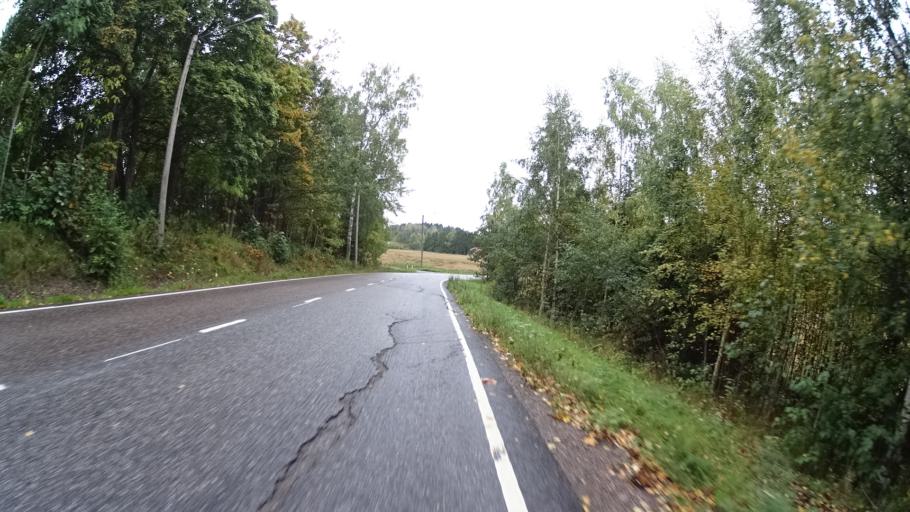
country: FI
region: Uusimaa
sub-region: Helsinki
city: Kauniainen
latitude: 60.2542
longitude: 24.7362
